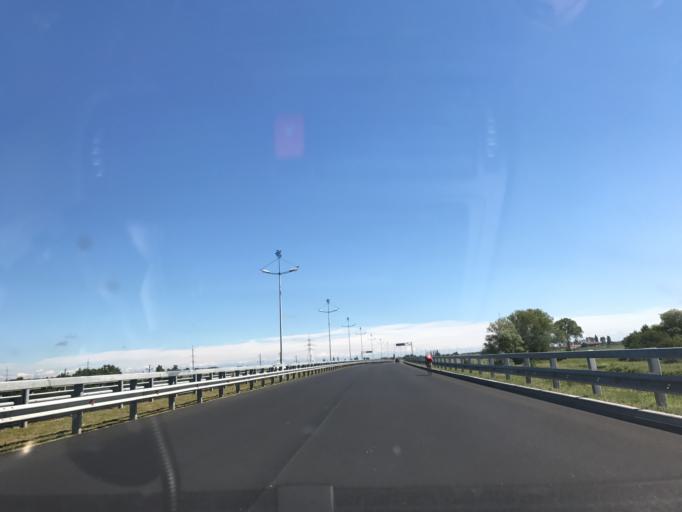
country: RU
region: Kaliningrad
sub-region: Zelenogradskiy Rayon
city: Zelenogradsk
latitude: 54.9200
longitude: 20.4481
